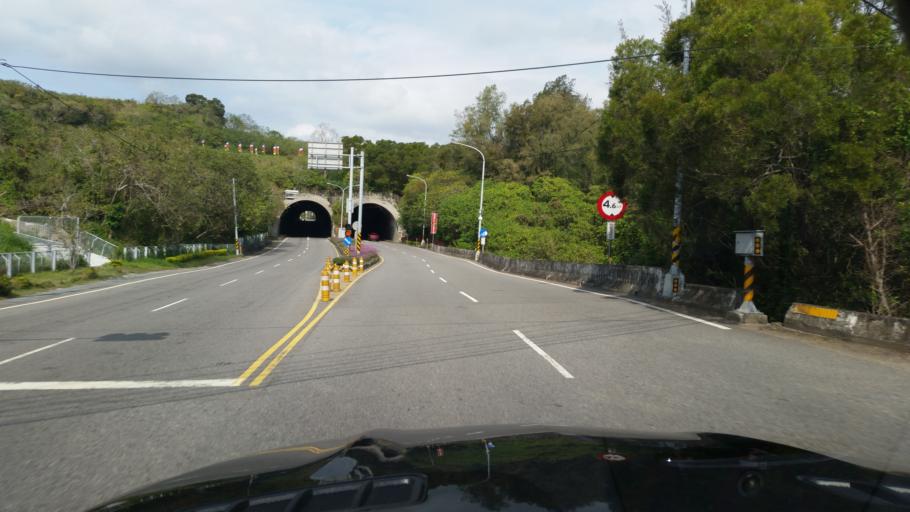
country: TW
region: Taiwan
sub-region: Miaoli
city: Miaoli
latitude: 24.6384
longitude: 120.8593
